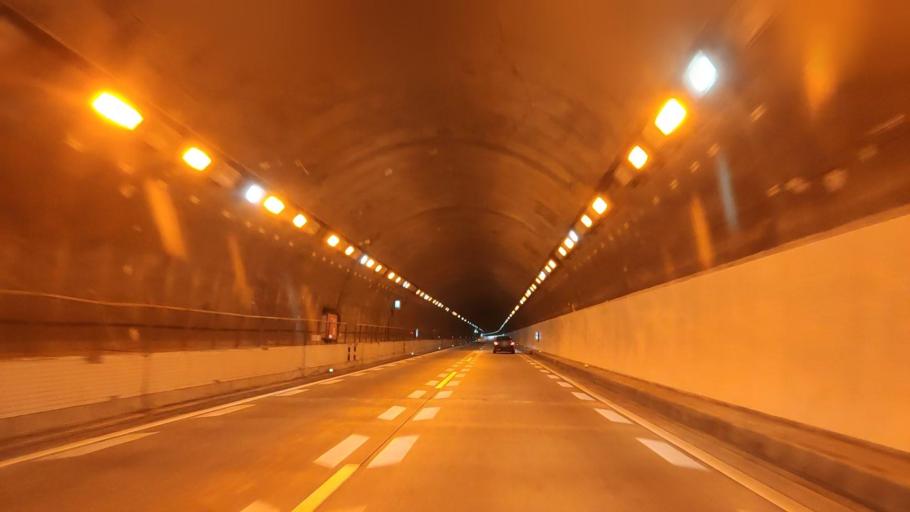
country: JP
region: Okayama
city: Kurashiki
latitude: 34.6085
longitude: 133.7307
